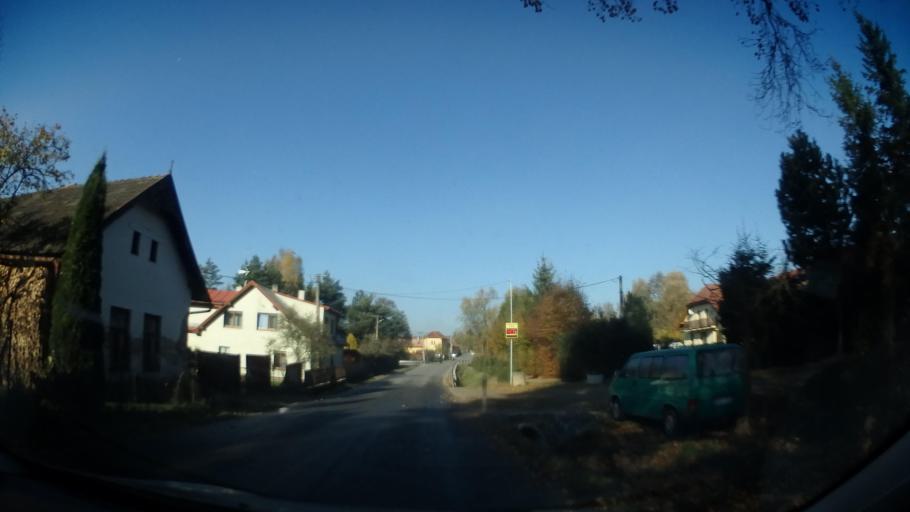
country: CZ
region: Vysocina
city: Zd'ar nad Sazavou Druhy
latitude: 49.6038
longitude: 15.9244
